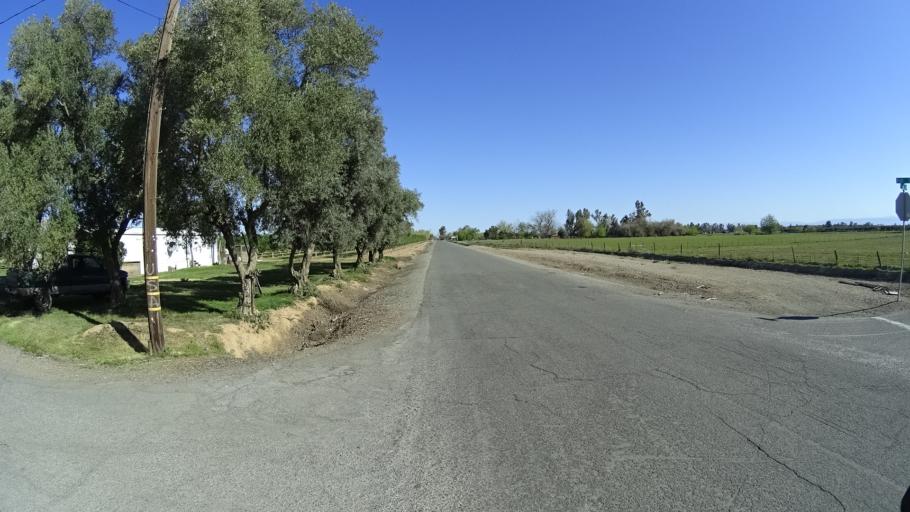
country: US
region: California
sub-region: Glenn County
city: Orland
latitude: 39.7476
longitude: -122.2392
